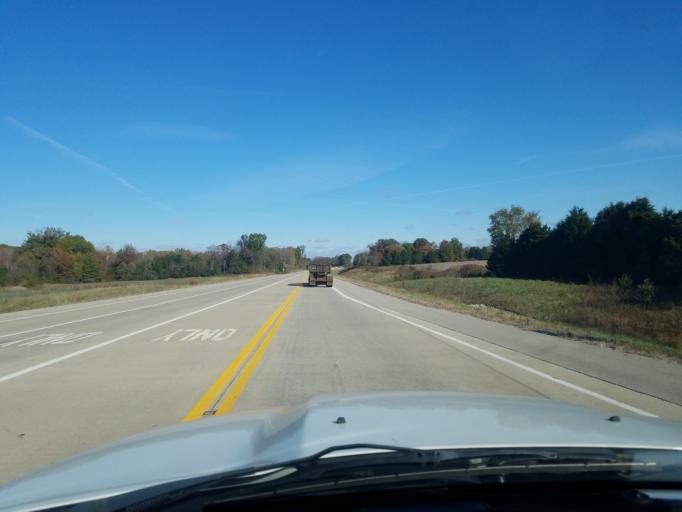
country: US
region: Indiana
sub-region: Jennings County
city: North Vernon
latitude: 39.0074
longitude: -85.6639
